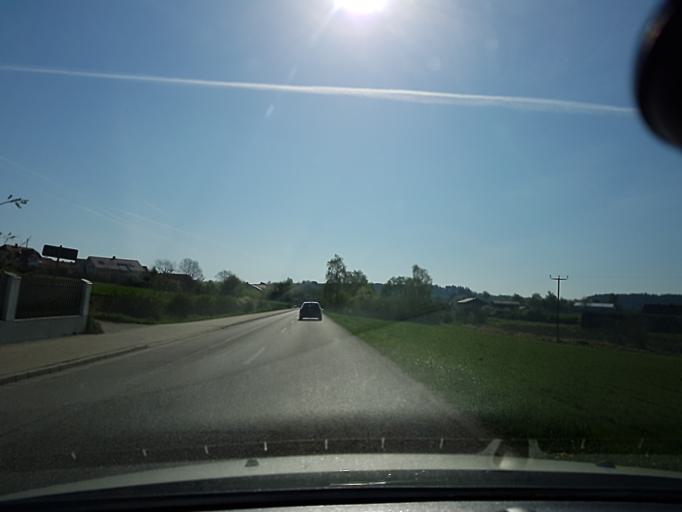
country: DE
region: Bavaria
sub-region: Lower Bavaria
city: Furth
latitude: 48.4040
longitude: 12.3866
